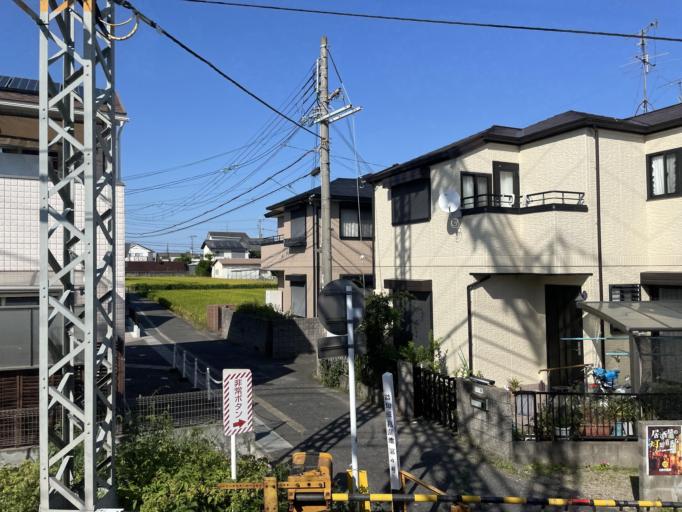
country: JP
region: Nara
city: Nara-shi
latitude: 34.6970
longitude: 135.7769
